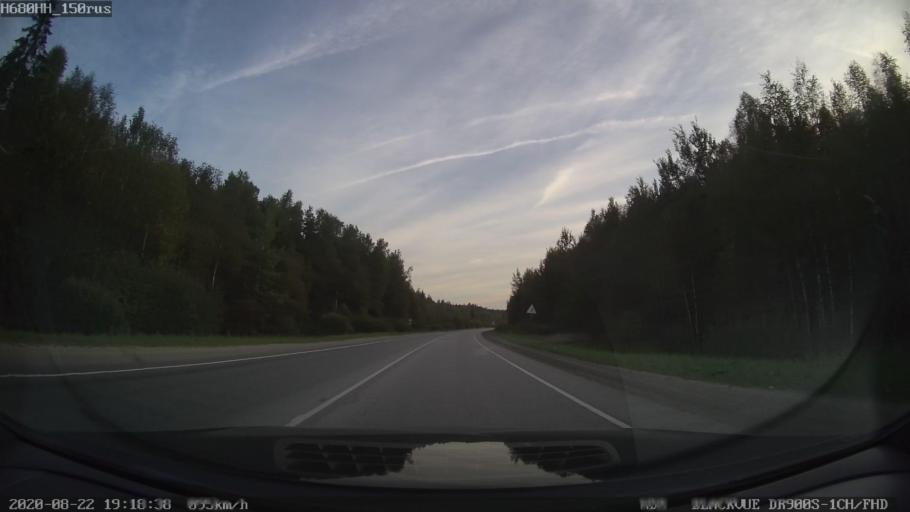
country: RU
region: Tverskaya
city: Sakharovo
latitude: 56.9322
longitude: 36.0032
